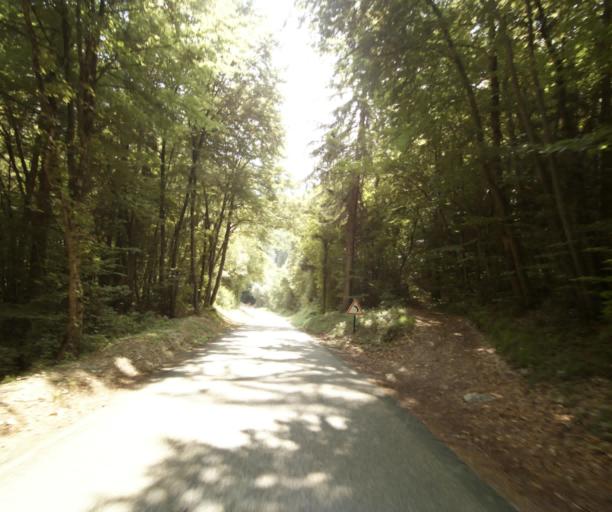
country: FR
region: Rhone-Alpes
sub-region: Departement de l'Isere
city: Le Sappey-en-Chartreuse
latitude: 45.2489
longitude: 5.7405
